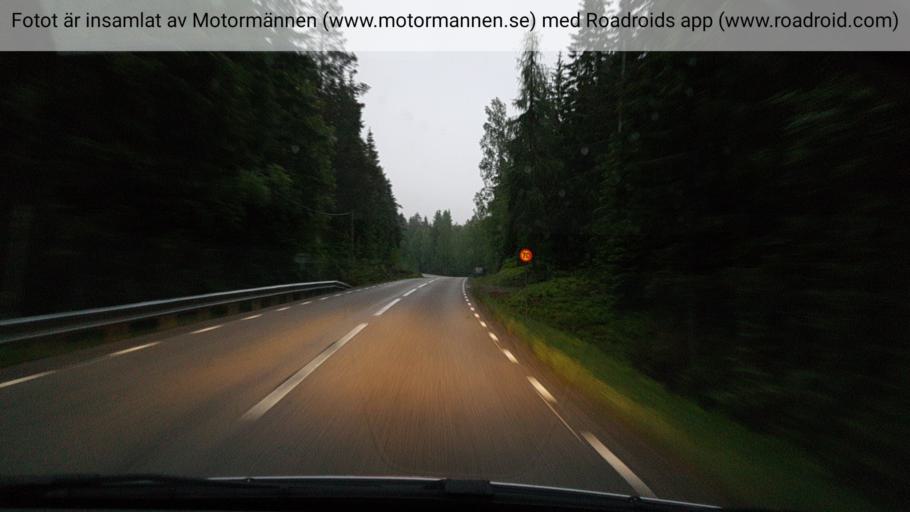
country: SE
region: OErebro
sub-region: Lindesbergs Kommun
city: Stora
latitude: 59.8954
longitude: 15.2754
